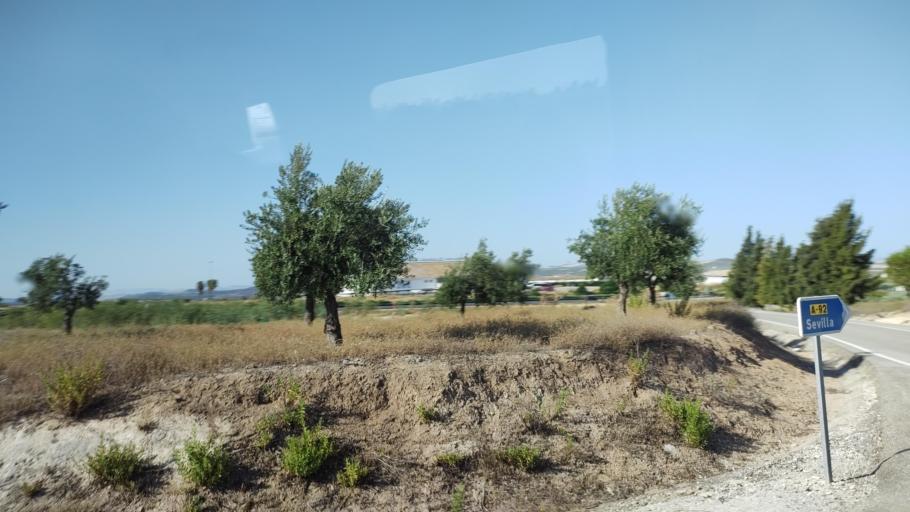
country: ES
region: Andalusia
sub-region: Provincia de Sevilla
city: Aguadulce
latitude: 37.2593
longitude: -4.9840
